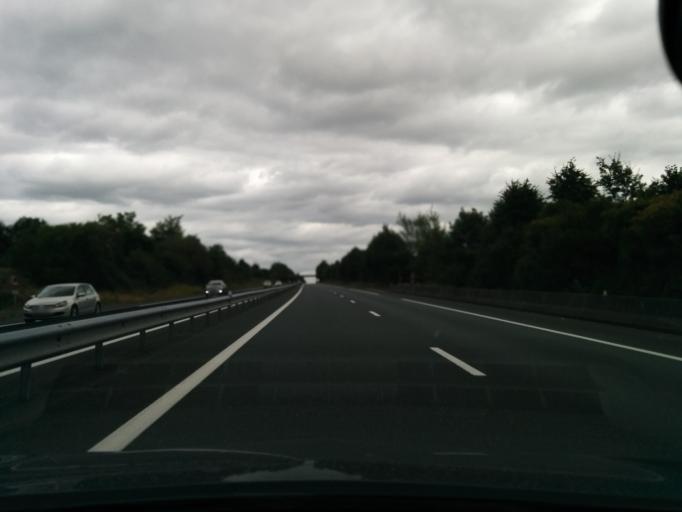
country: FR
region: Limousin
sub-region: Departement de la Haute-Vienne
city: Saint-Sulpice-les-Feuilles
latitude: 46.3820
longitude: 1.4481
